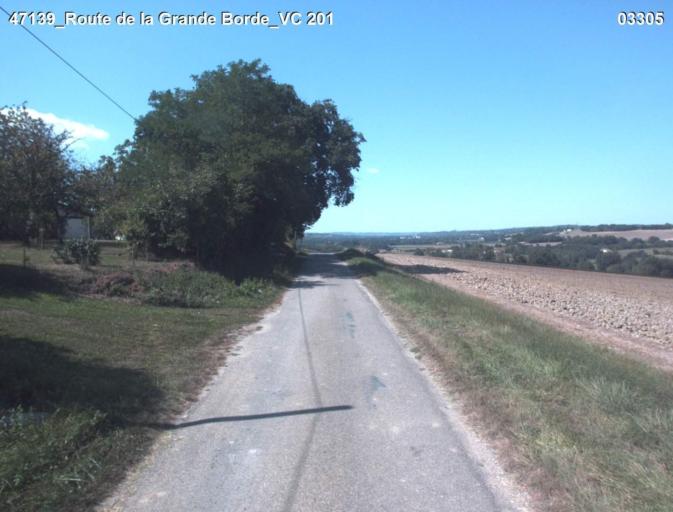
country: FR
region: Aquitaine
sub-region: Departement du Lot-et-Garonne
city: Nerac
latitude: 44.0884
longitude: 0.3804
